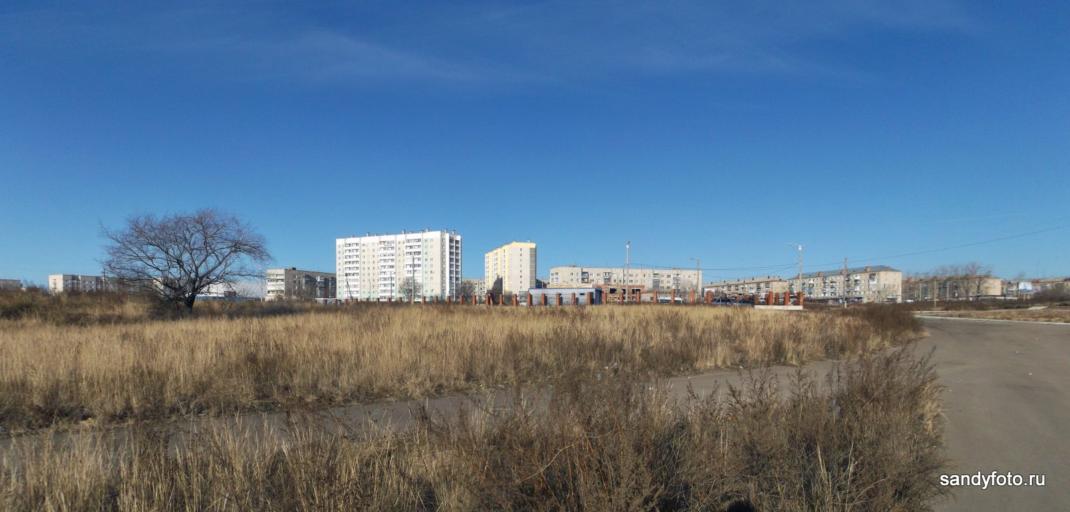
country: RU
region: Chelyabinsk
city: Troitsk
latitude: 54.0749
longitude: 61.5299
